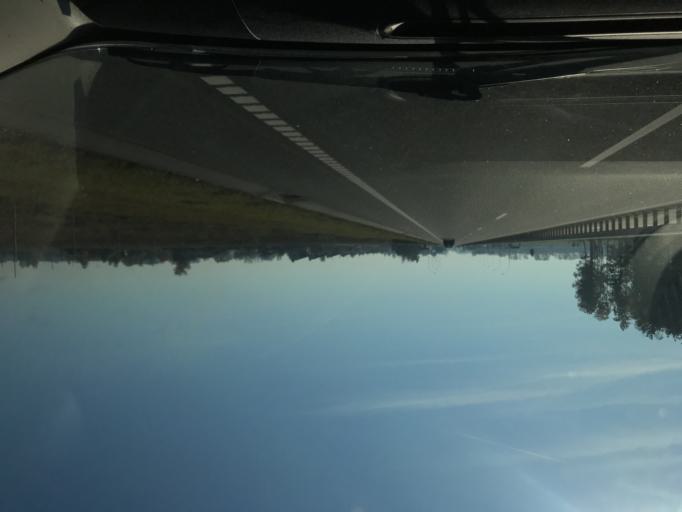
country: BY
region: Minsk
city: Slutsk
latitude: 53.2316
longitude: 27.5506
